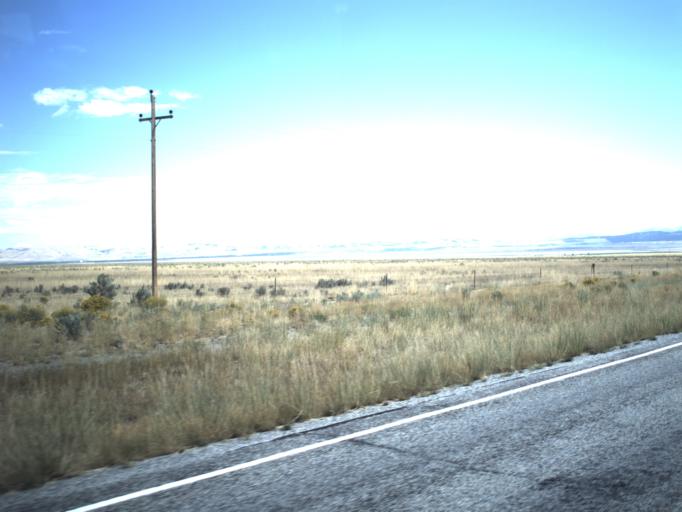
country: US
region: Idaho
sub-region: Oneida County
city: Malad City
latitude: 41.9656
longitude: -113.0171
